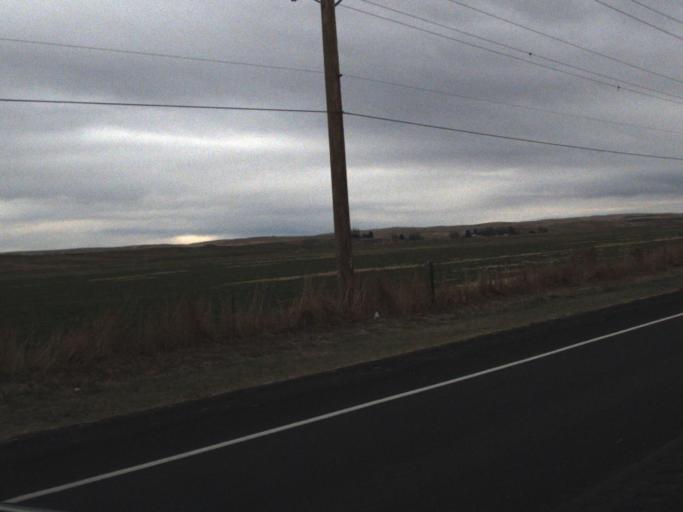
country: US
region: Washington
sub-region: Walla Walla County
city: Garrett
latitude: 46.0503
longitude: -118.6262
